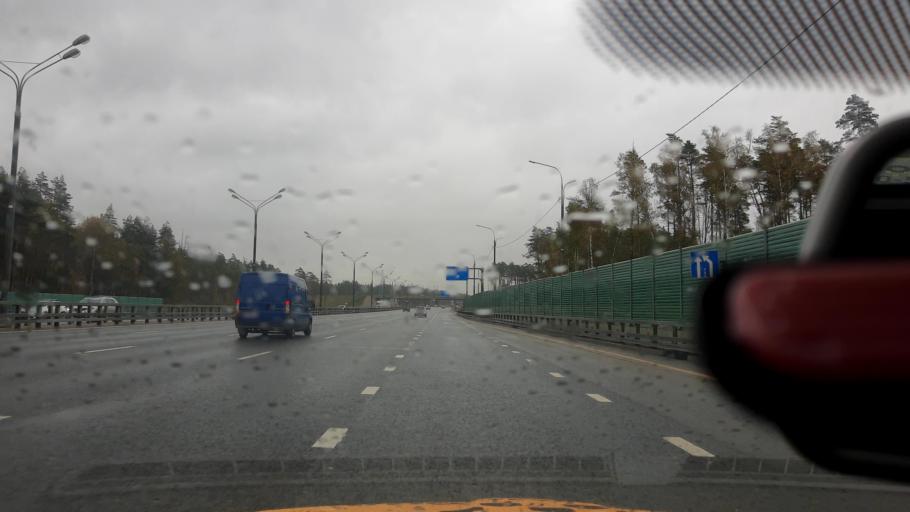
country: RU
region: Moskovskaya
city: Zhavoronki
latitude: 55.6147
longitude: 37.0900
